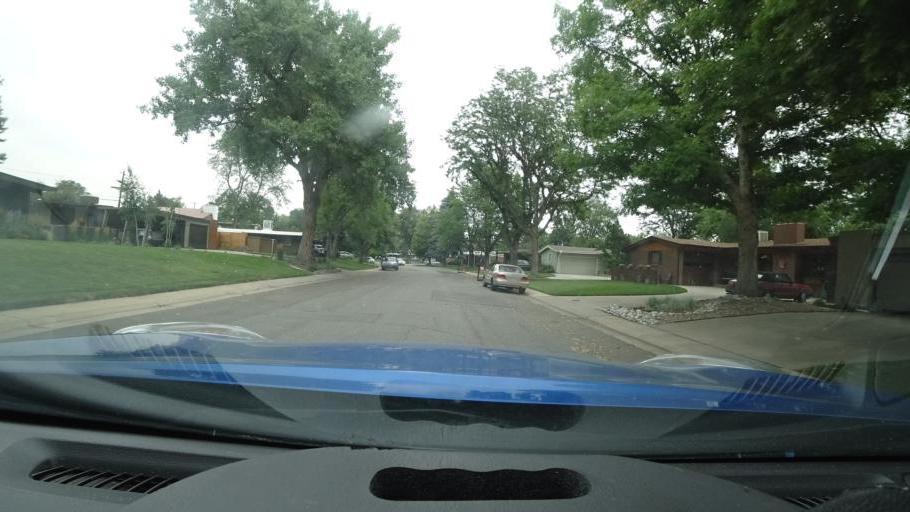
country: US
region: Colorado
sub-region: Arapahoe County
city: Glendale
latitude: 39.6837
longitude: -104.9198
